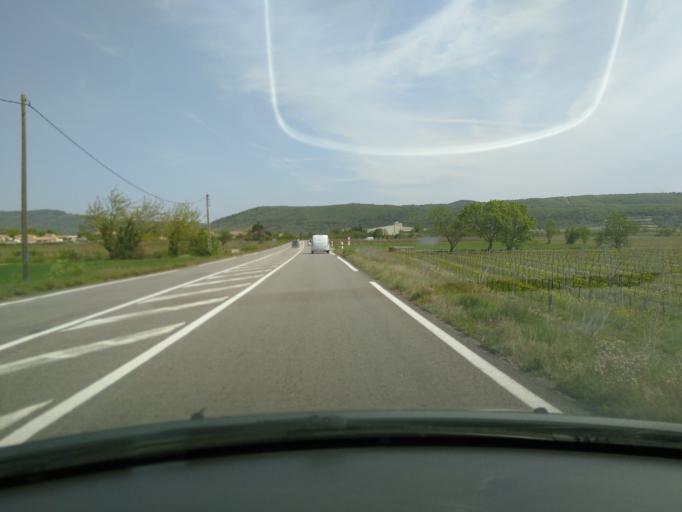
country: FR
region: Rhone-Alpes
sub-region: Departement de l'Ardeche
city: Alba-la-Romaine
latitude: 44.5675
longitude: 4.5950
